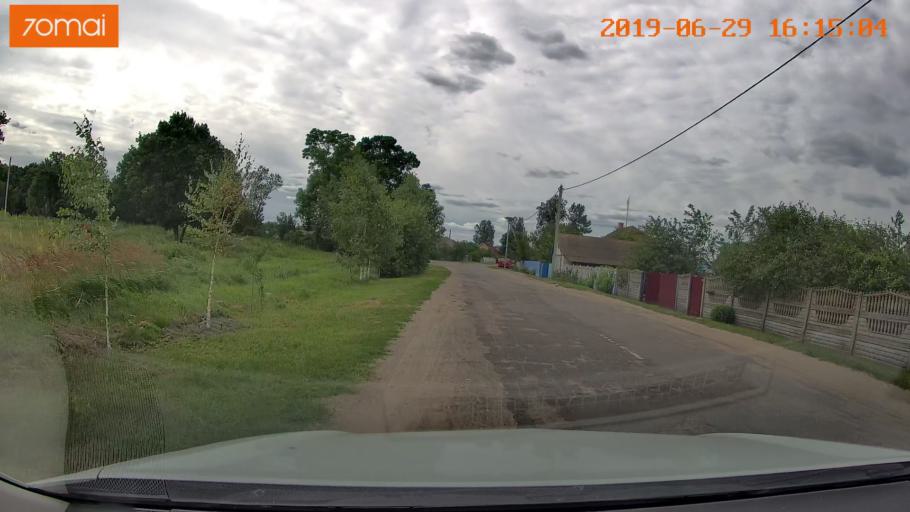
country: BY
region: Brest
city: Luninyets
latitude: 52.1999
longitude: 27.0159
